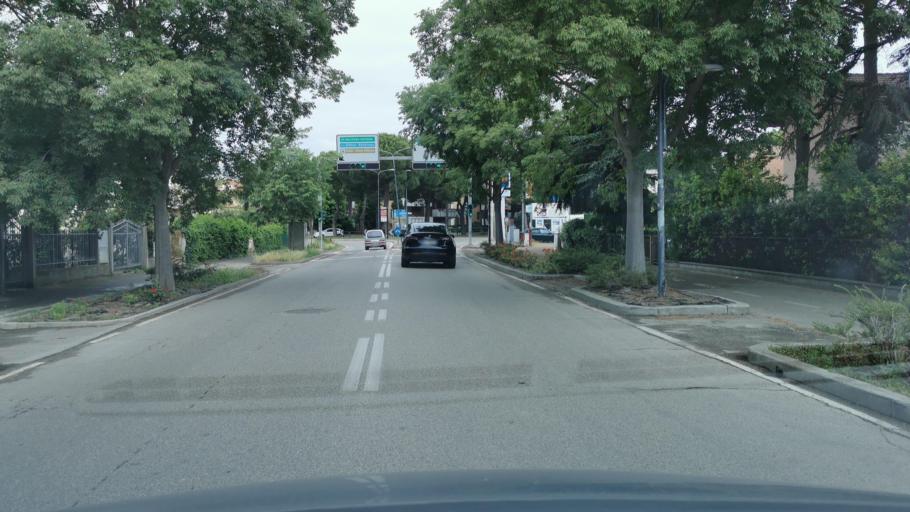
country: IT
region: Emilia-Romagna
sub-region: Provincia di Ravenna
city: Cervia
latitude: 44.2659
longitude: 12.3462
